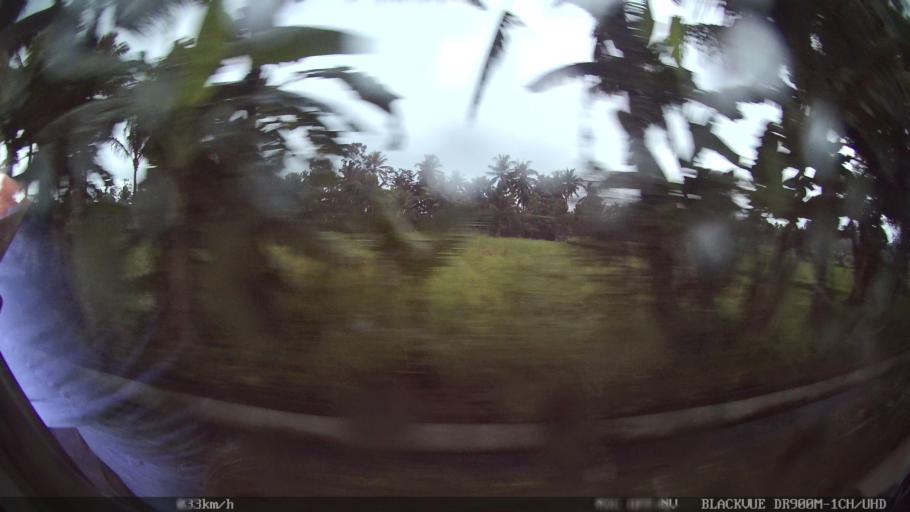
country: ID
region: Bali
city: Kekeran
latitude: -8.4845
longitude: 115.1870
